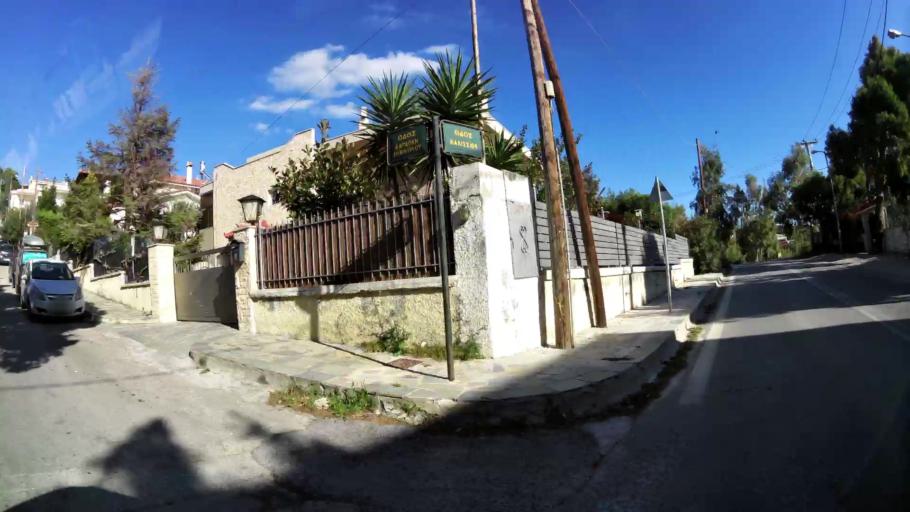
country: GR
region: Attica
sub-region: Nomarchia Athinas
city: Penteli
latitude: 38.0439
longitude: 23.8817
